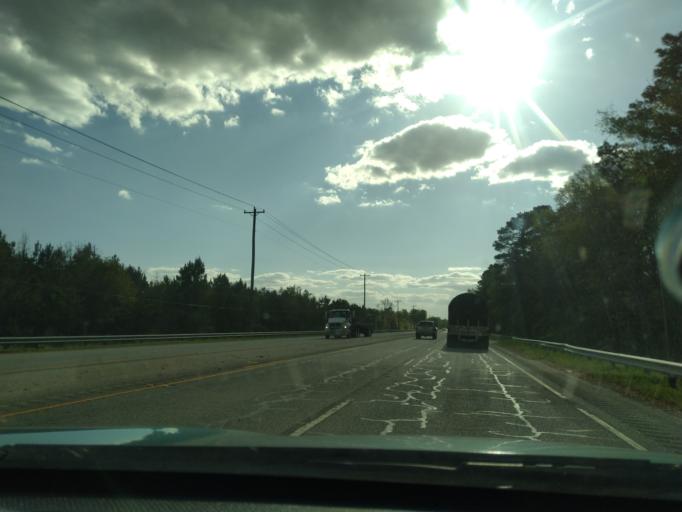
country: US
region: South Carolina
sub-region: Williamsburg County
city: Kingstree
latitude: 33.6604
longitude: -79.8447
